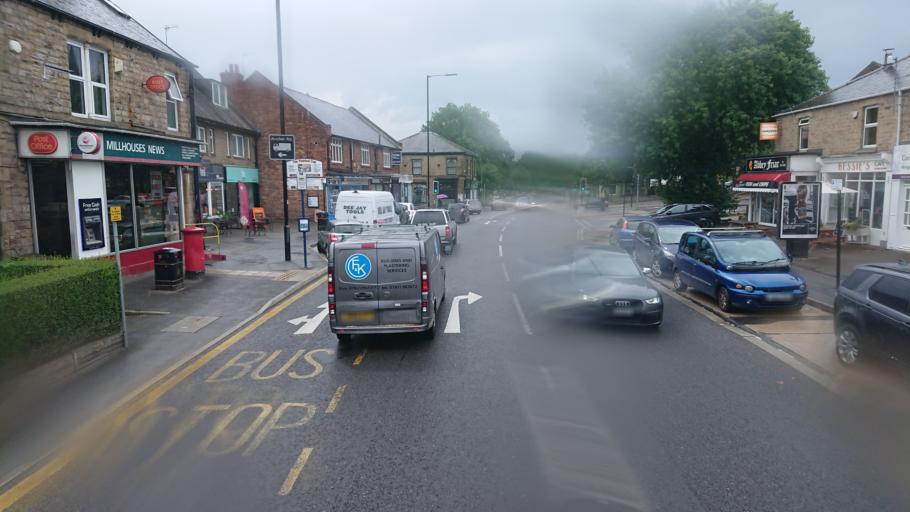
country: GB
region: England
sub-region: Sheffield
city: Sheffield
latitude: 53.3465
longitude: -1.4961
